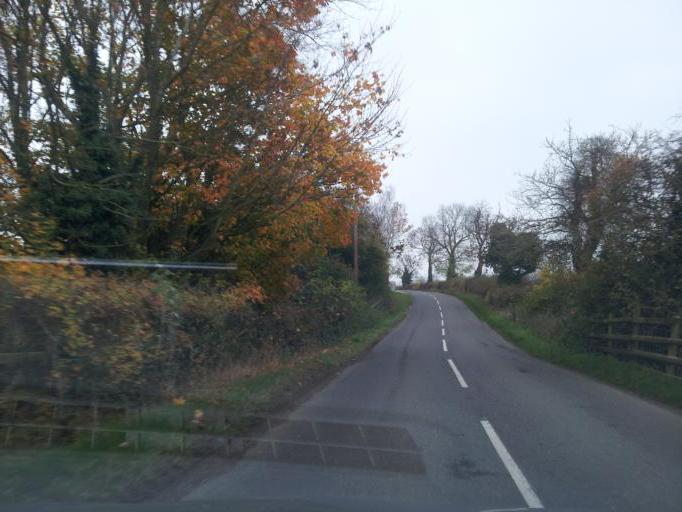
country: GB
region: England
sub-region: Milton Keynes
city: Shenley Church End
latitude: 51.9896
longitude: -0.8279
